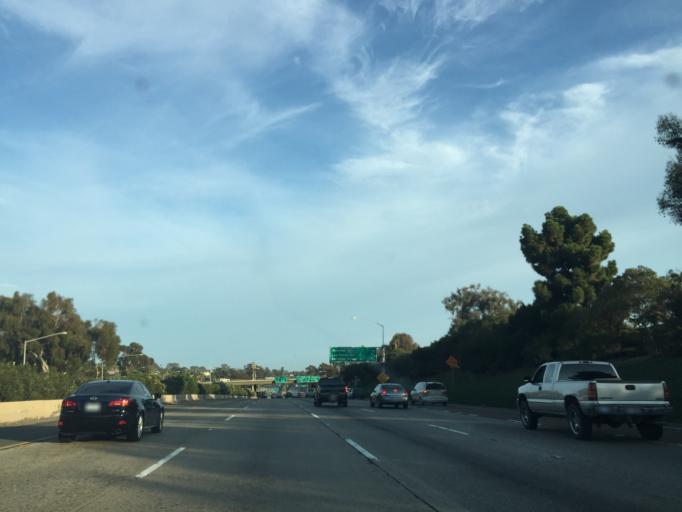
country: US
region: California
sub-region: San Diego County
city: Carlsbad
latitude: 33.1793
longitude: -117.3534
